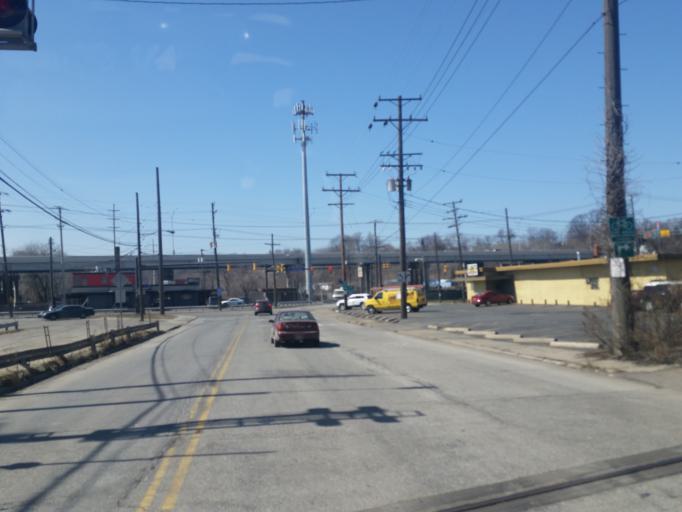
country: US
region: Ohio
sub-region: Cuyahoga County
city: Brooklyn Heights
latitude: 41.4474
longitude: -81.6866
